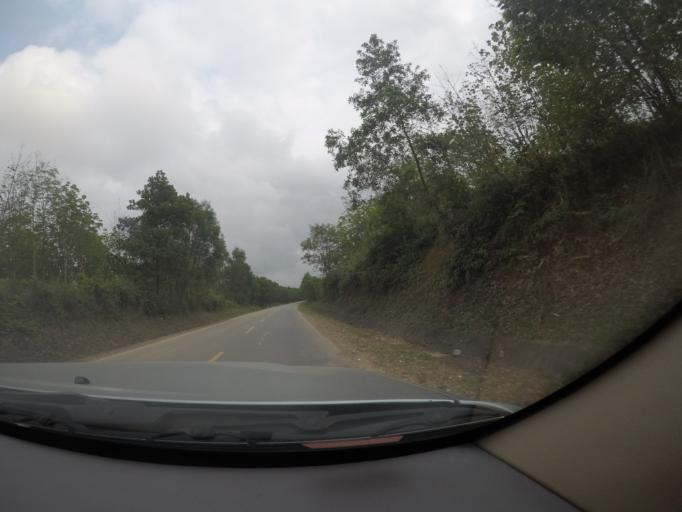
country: VN
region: Quang Tri
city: Ho Xa
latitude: 16.9831
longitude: 106.9316
